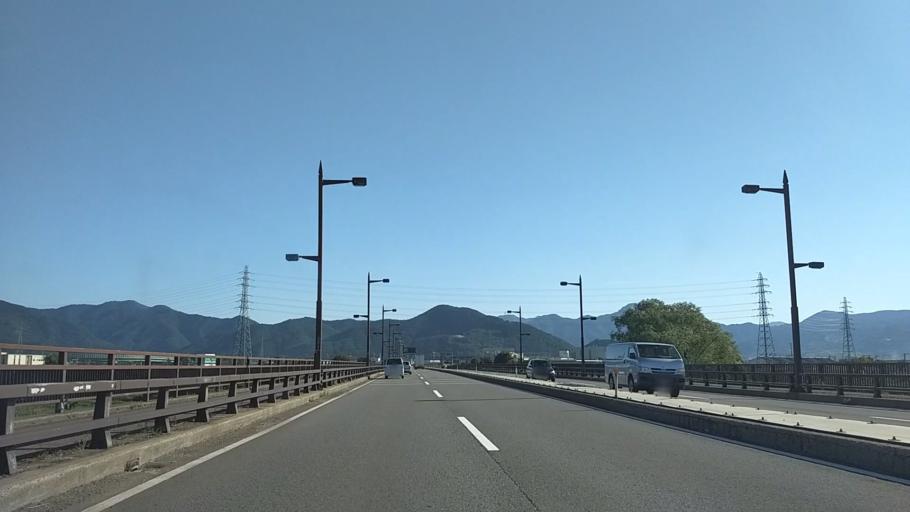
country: JP
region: Nagano
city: Nagano-shi
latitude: 36.5588
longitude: 138.1384
